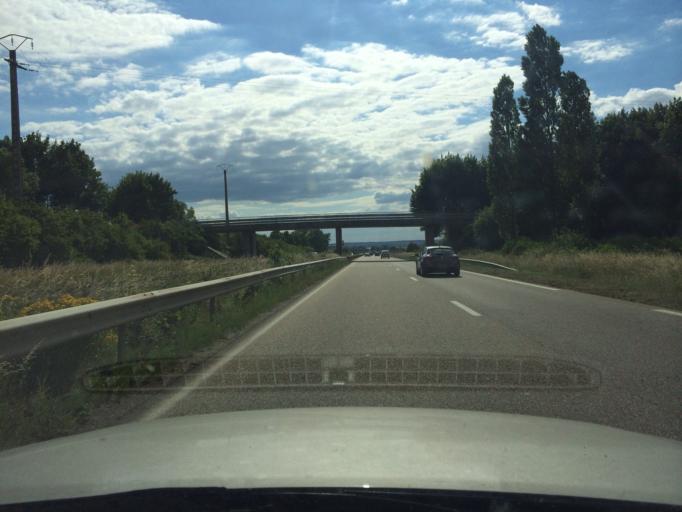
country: FR
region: Lorraine
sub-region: Departement de la Moselle
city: Phalsbourg
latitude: 48.7553
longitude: 7.1986
